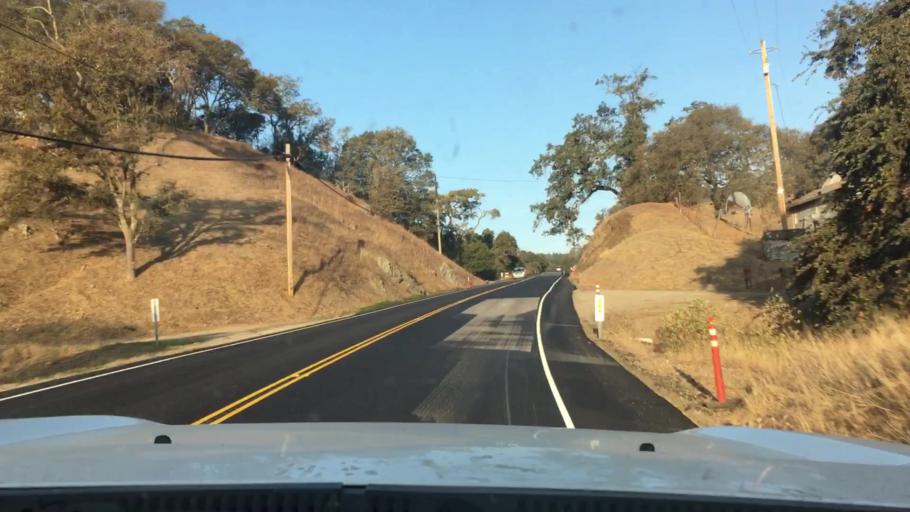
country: US
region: California
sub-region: San Luis Obispo County
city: Atascadero
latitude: 35.4518
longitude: -120.7083
